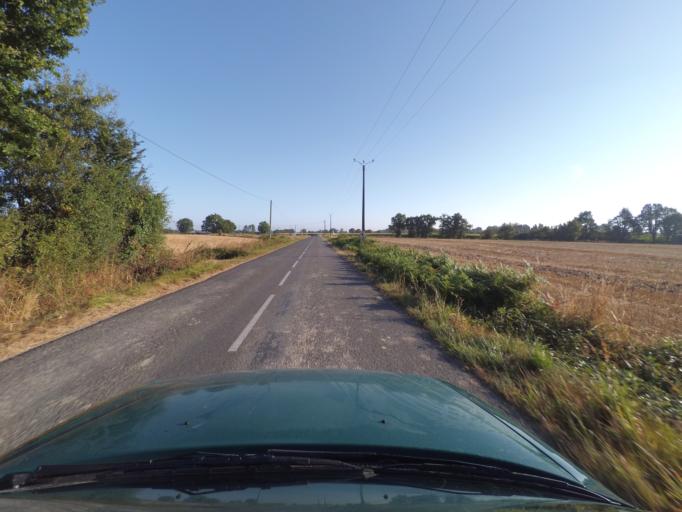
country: FR
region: Pays de la Loire
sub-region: Departement de la Loire-Atlantique
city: La Planche
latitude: 47.0041
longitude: -1.4550
